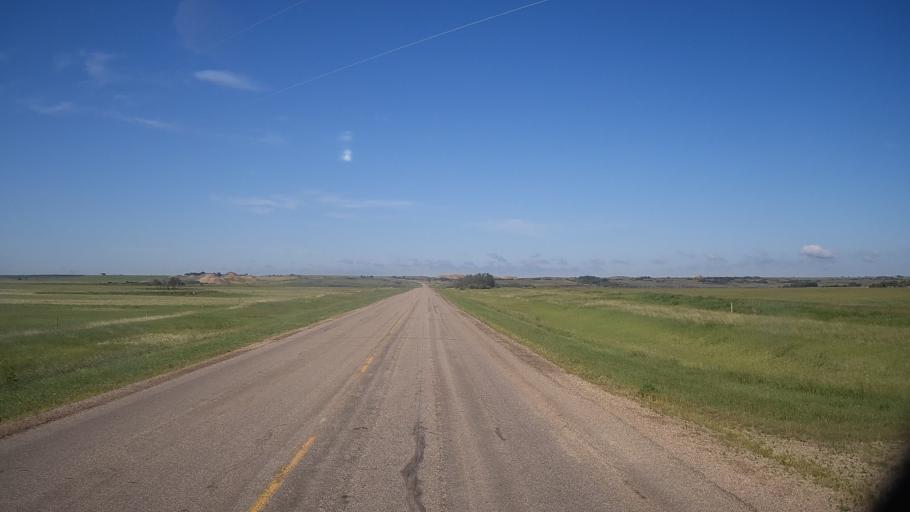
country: CA
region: Saskatchewan
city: Watrous
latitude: 51.7185
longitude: -105.3611
